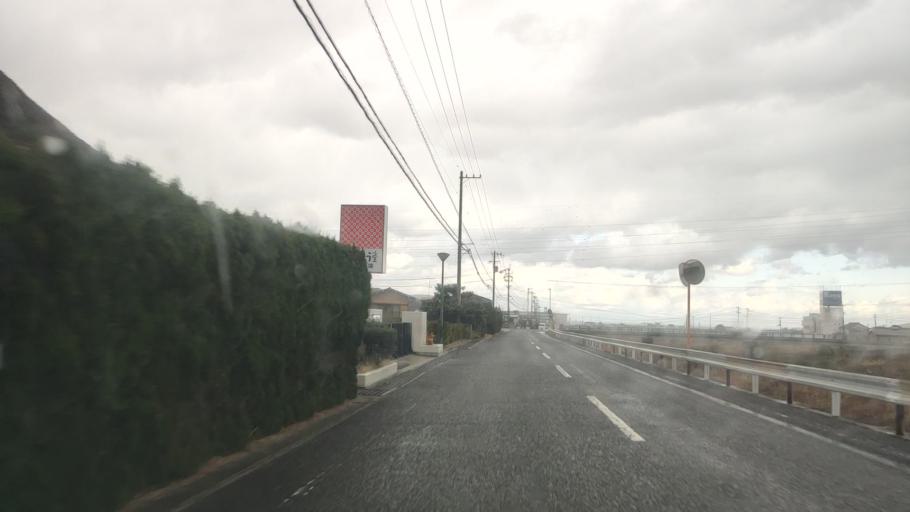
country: JP
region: Tokushima
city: Ishii
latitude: 34.2118
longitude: 134.4051
